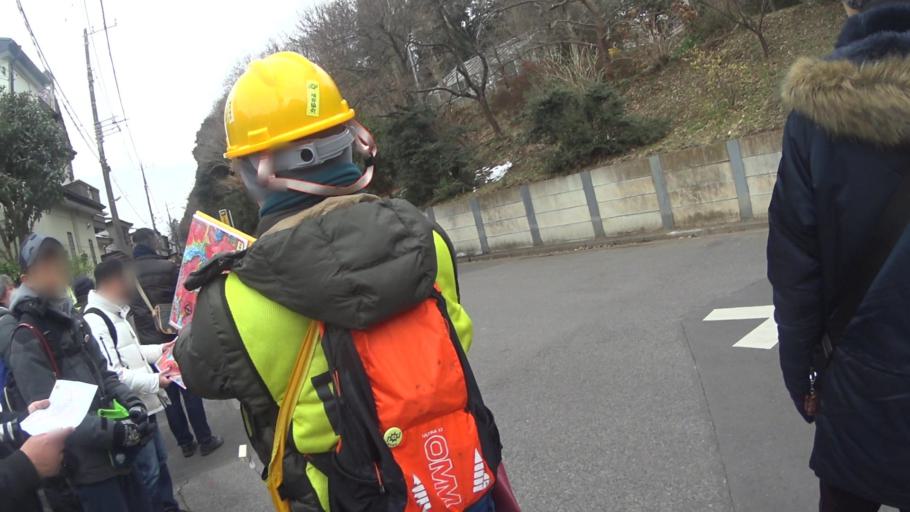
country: JP
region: Chiba
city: Funabashi
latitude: 35.7472
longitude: 139.9851
